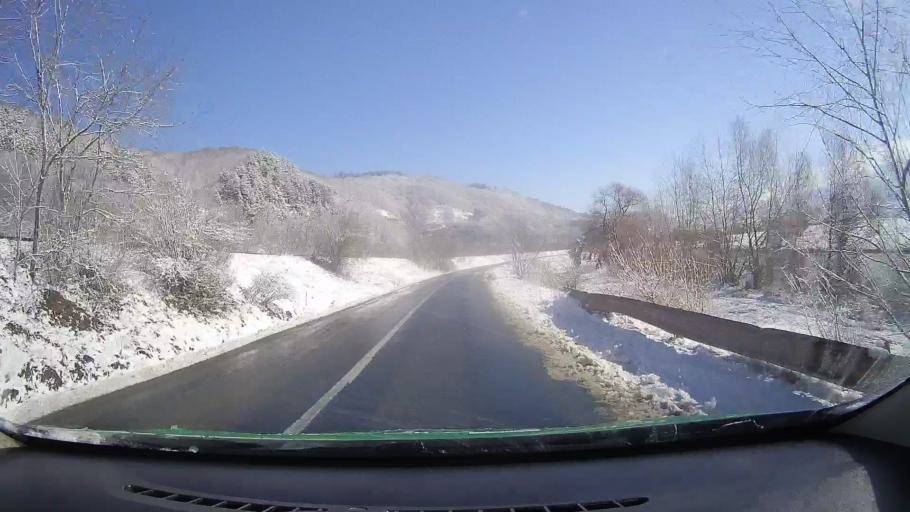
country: RO
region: Sibiu
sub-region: Comuna Talmaciu
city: Talmaciu
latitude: 45.6612
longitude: 24.2804
